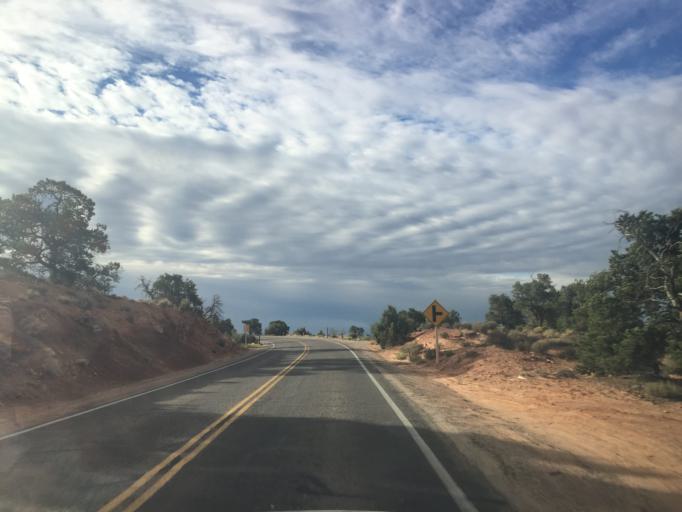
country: US
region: Utah
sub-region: Grand County
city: Moab
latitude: 38.7698
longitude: -109.5893
